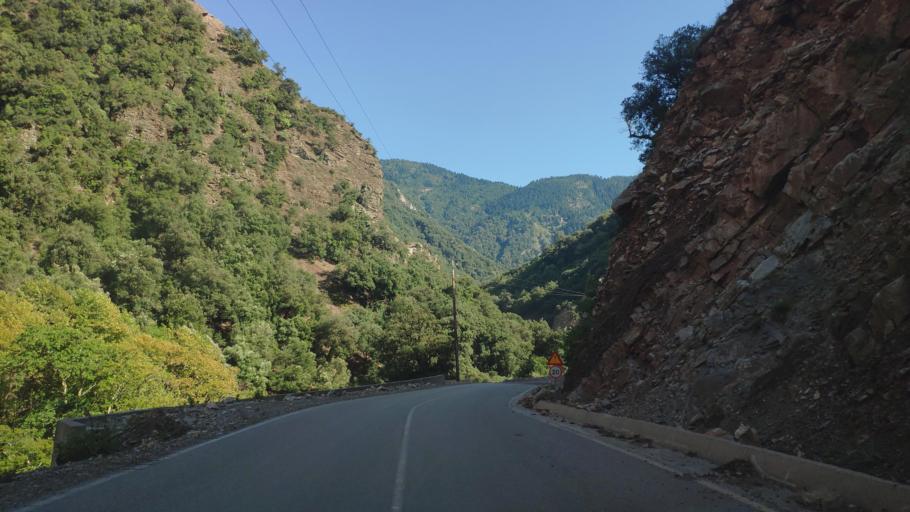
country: GR
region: Central Greece
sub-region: Nomos Evrytanias
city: Kerasochori
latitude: 39.0735
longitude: 21.6006
